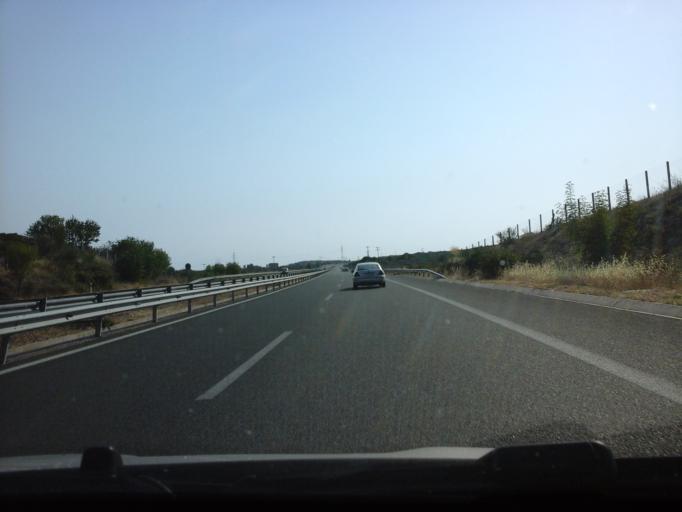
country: GR
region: East Macedonia and Thrace
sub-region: Nomos Evrou
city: Alexandroupoli
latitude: 40.8662
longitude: 25.7678
